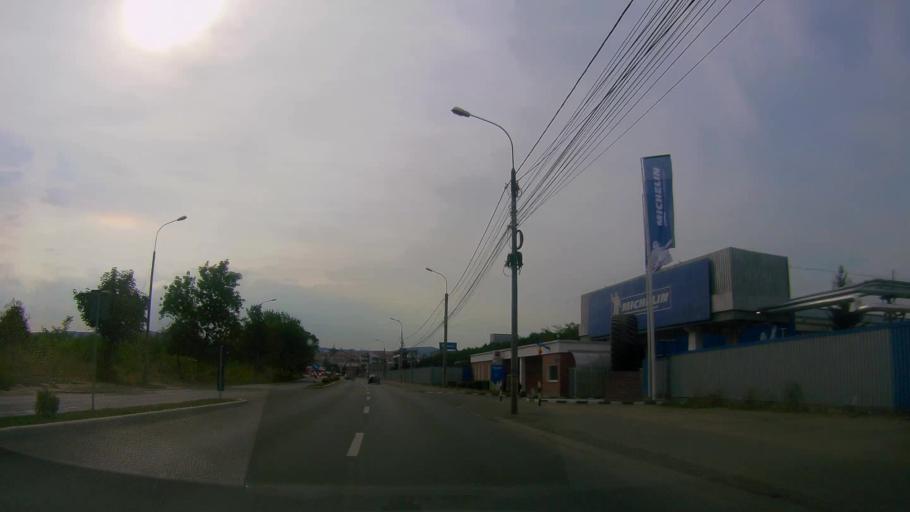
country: RO
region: Salaj
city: Zalau
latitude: 47.2089
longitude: 23.0446
